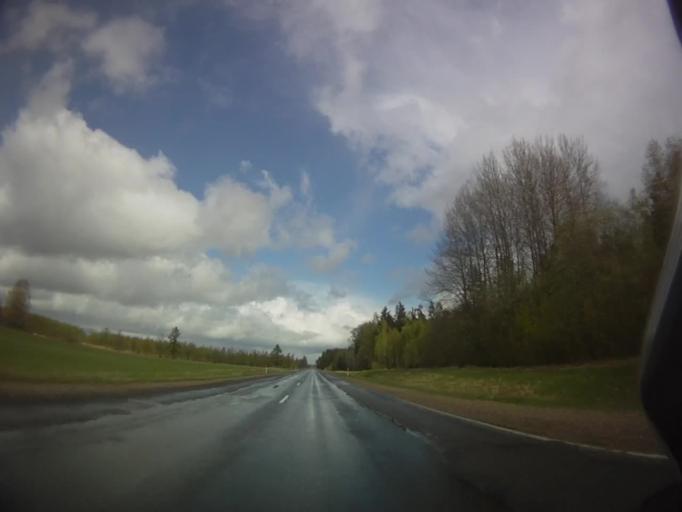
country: LV
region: Koceni
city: Koceni
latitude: 57.4448
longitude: 25.2185
